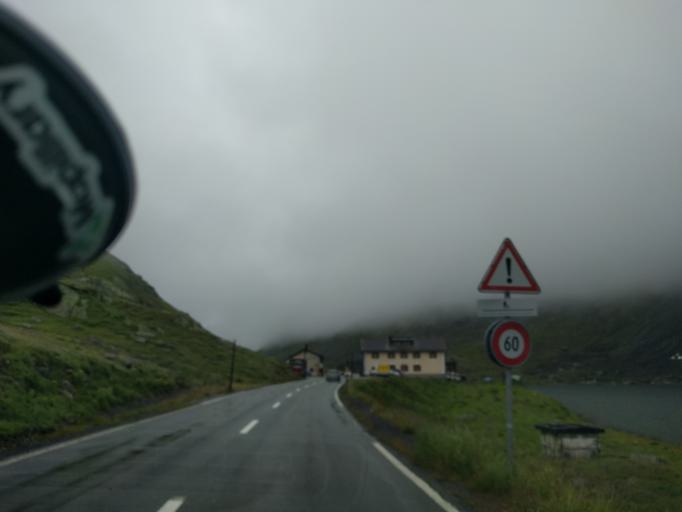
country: CH
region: Grisons
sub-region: Praettigau/Davos District
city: Davos
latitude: 46.7514
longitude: 9.9463
